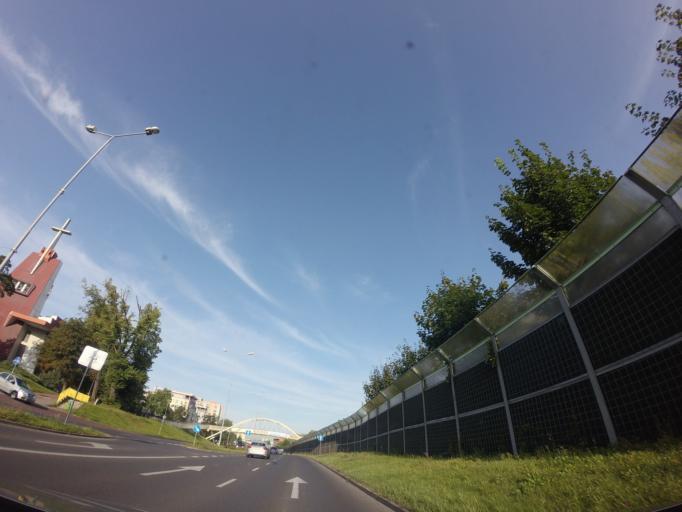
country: PL
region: West Pomeranian Voivodeship
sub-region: Szczecin
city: Szczecin
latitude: 53.4540
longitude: 14.5580
